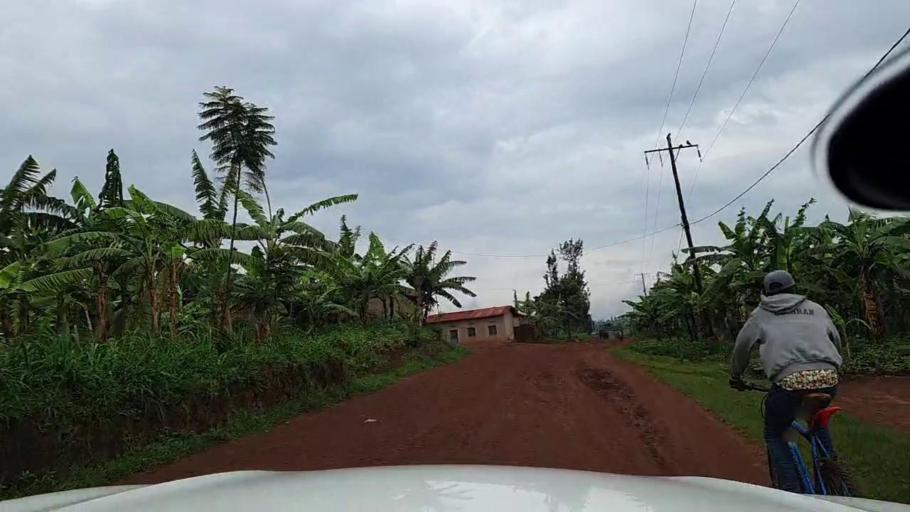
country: RW
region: Kigali
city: Kigali
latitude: -1.9161
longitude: 29.8985
